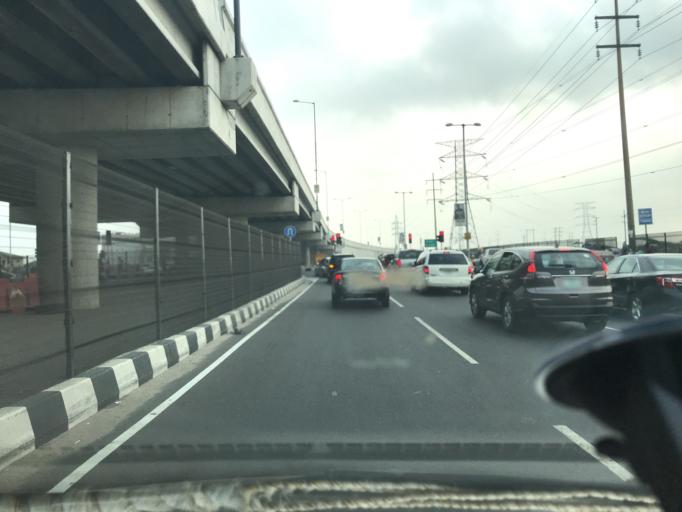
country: NG
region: Lagos
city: Ikoyi
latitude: 6.4673
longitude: 3.5643
